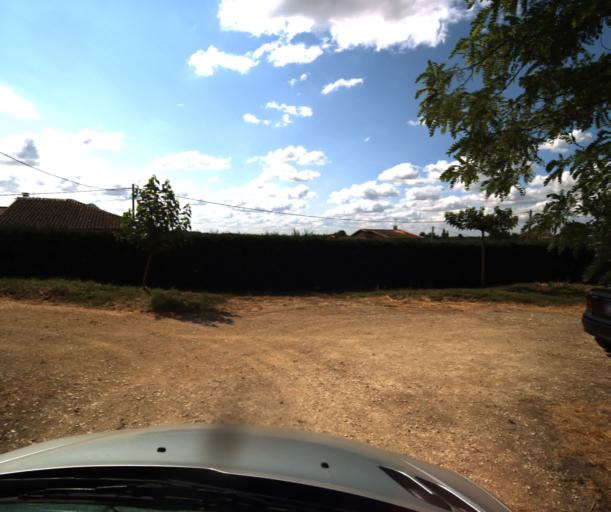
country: FR
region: Midi-Pyrenees
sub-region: Departement du Tarn-et-Garonne
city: Finhan
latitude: 43.9116
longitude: 1.2714
